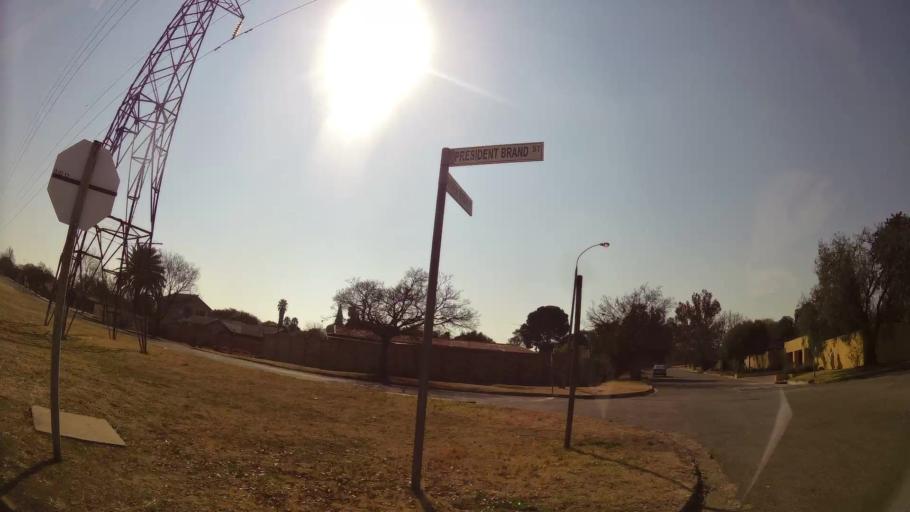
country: ZA
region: Gauteng
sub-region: Ekurhuleni Metropolitan Municipality
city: Boksburg
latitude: -26.2308
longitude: 28.2771
